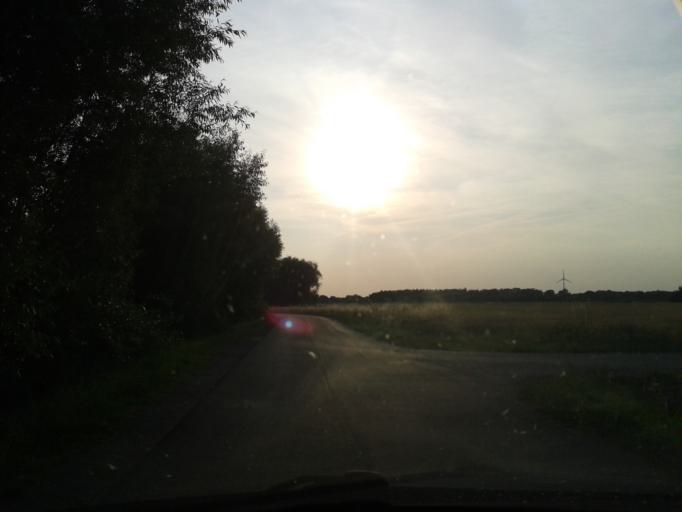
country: DE
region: North Rhine-Westphalia
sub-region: Regierungsbezirk Detmold
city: Paderborn
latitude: 51.7307
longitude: 8.6785
